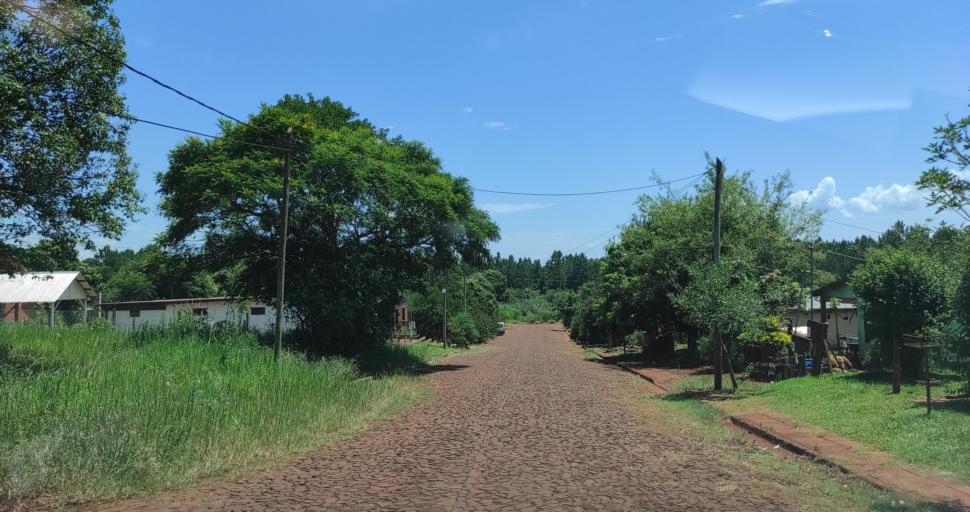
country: AR
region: Misiones
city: Ruiz de Montoya
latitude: -26.9699
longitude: -55.0486
